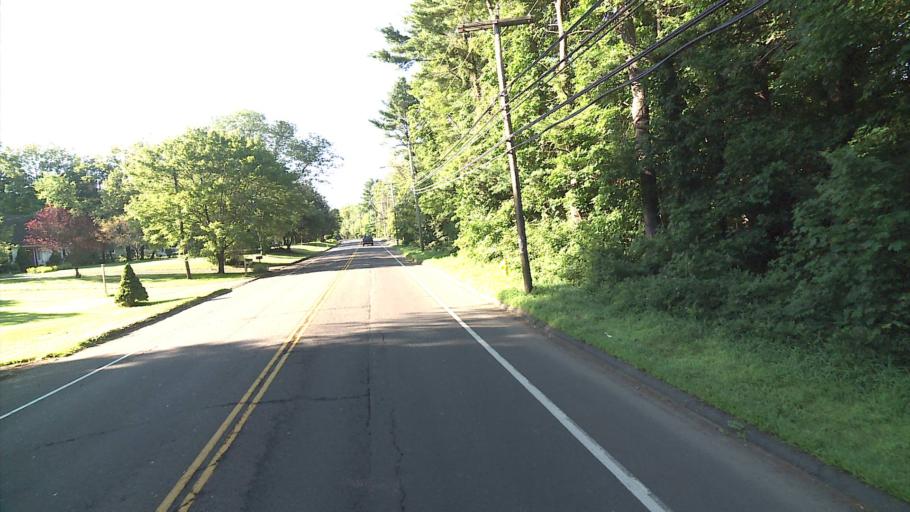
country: US
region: Connecticut
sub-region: New Haven County
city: Hamden
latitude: 41.4410
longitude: -72.9107
